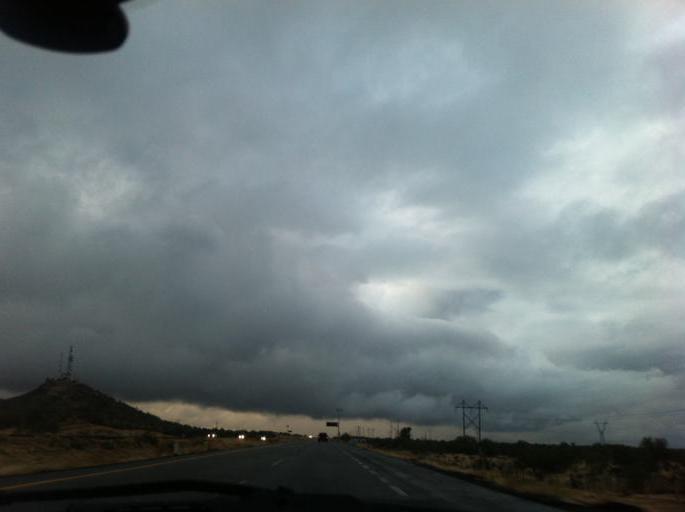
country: MX
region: Sonora
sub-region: San Miguel de Horcasitas
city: Las Mercedes [Agropecuaria]
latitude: 29.7575
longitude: -111.0553
